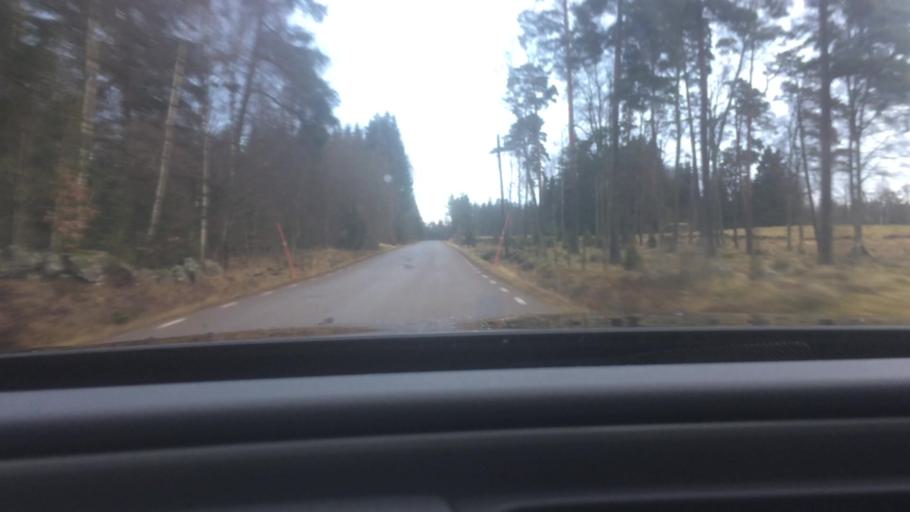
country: SE
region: Vaestra Goetaland
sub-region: Falkopings Kommun
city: Falkoeping
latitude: 57.9951
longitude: 13.4747
